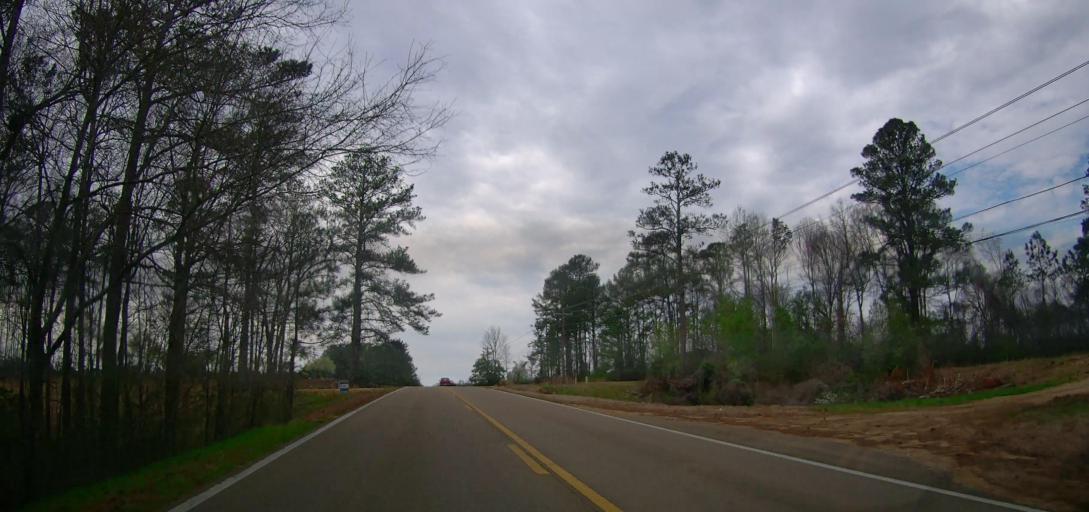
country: US
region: Mississippi
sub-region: Itawamba County
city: Fulton
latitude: 34.2763
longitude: -88.3573
